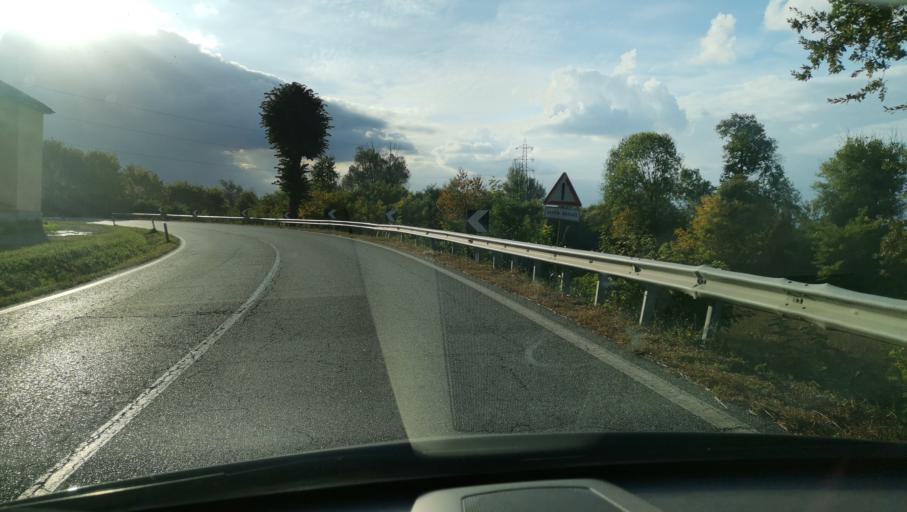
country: IT
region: Piedmont
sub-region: Provincia di Torino
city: Castagneto Po
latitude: 45.1760
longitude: 7.8807
